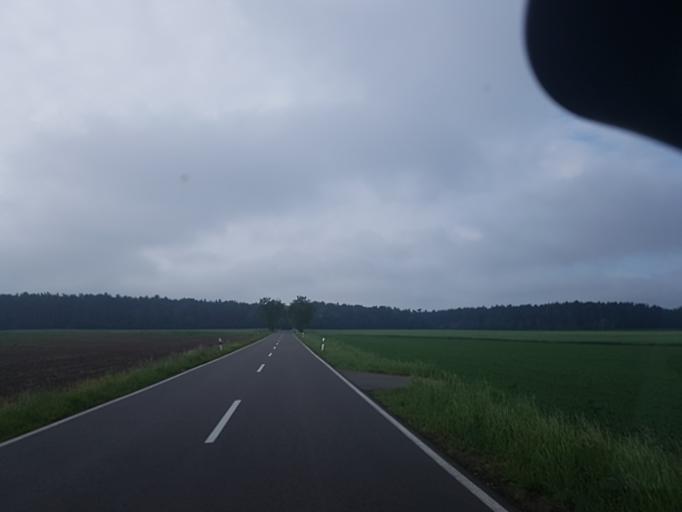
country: DE
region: Saxony-Anhalt
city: Klieken
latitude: 52.0044
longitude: 12.3706
